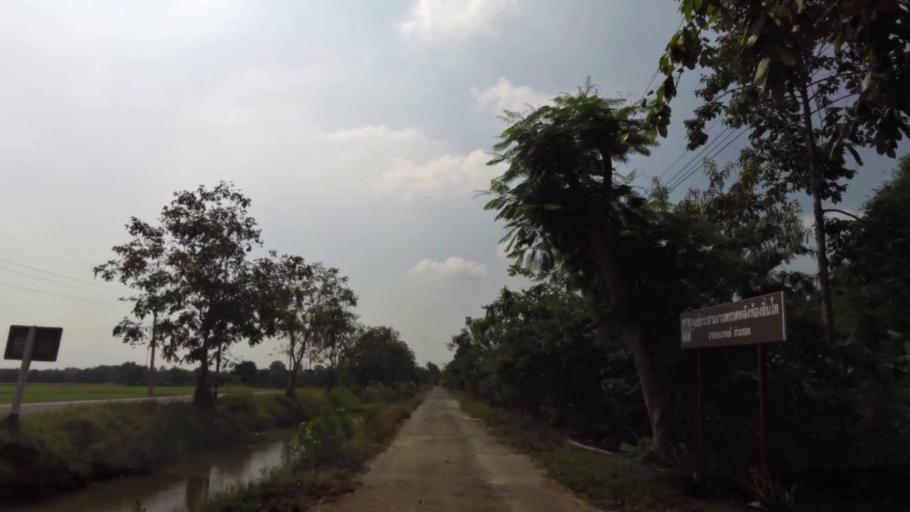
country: TH
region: Ang Thong
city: Pho Thong
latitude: 14.6106
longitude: 100.3956
